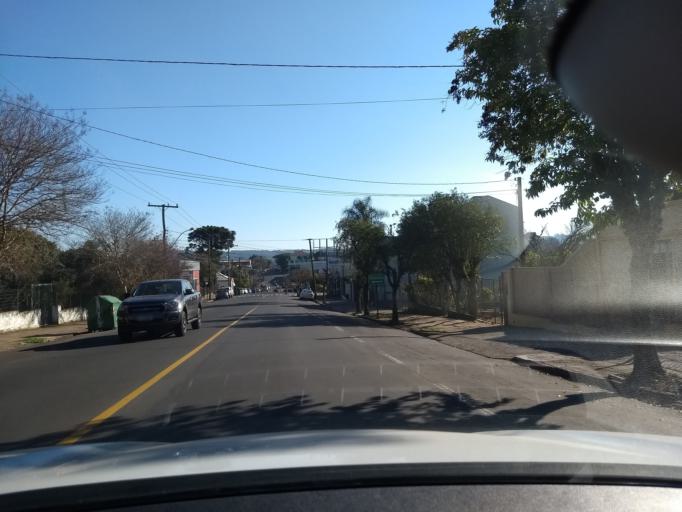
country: BR
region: Rio Grande do Sul
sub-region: Santa Cruz Do Sul
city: Santa Cruz do Sul
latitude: -29.7192
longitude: -52.4415
